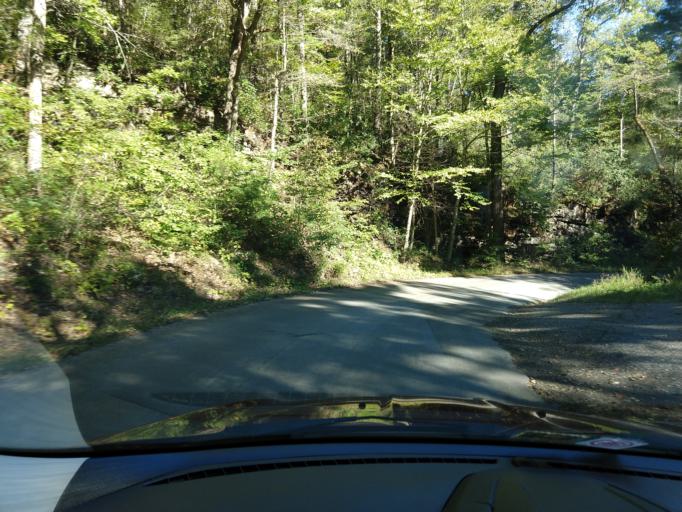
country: US
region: Virginia
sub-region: Alleghany County
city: Clifton Forge
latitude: 37.8578
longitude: -79.8716
